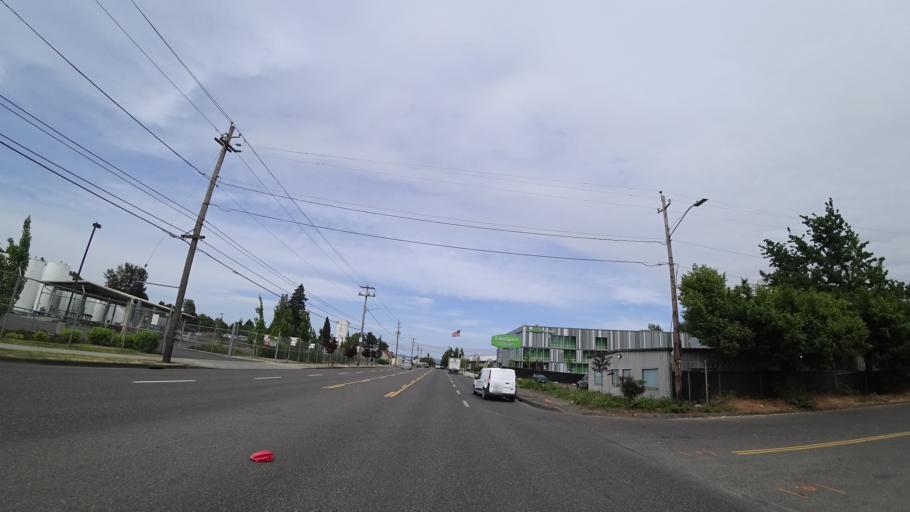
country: US
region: Oregon
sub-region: Multnomah County
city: Portland
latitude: 45.5748
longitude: -122.6355
